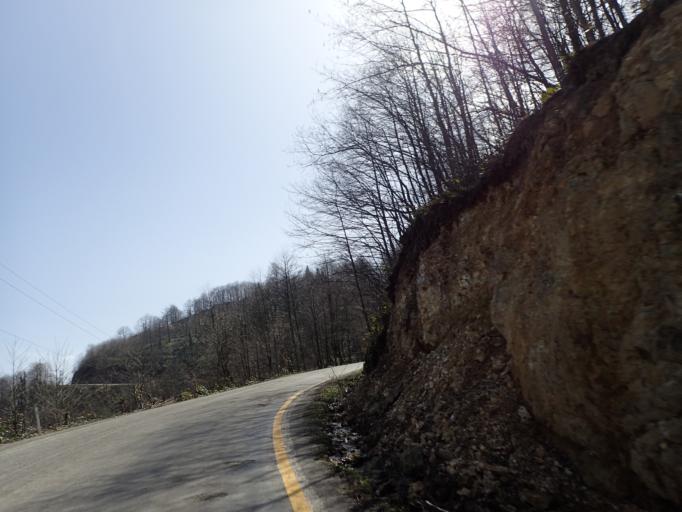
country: TR
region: Ordu
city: Kabaduz
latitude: 40.8242
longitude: 37.8991
